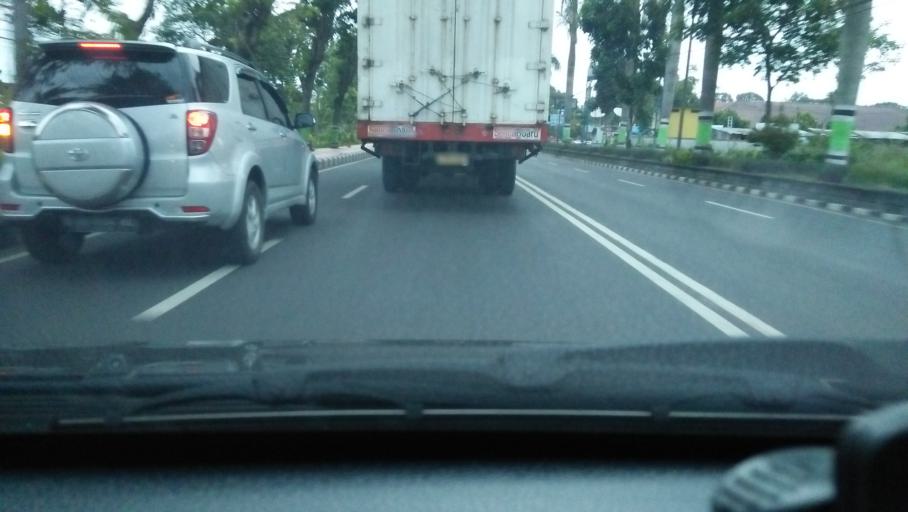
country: ID
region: Central Java
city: Magelang
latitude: -7.4375
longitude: 110.2275
